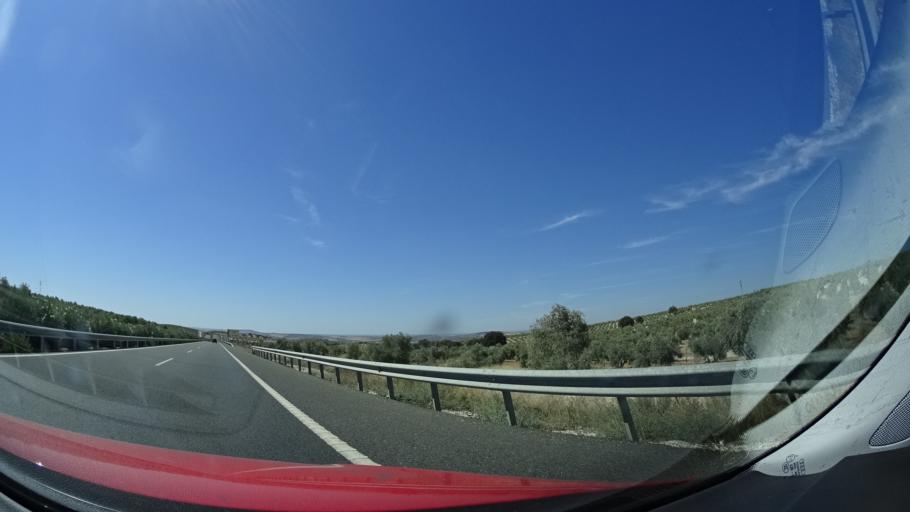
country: ES
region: Andalusia
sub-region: Provincia de Sevilla
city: Gilena
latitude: 37.2790
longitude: -4.9290
